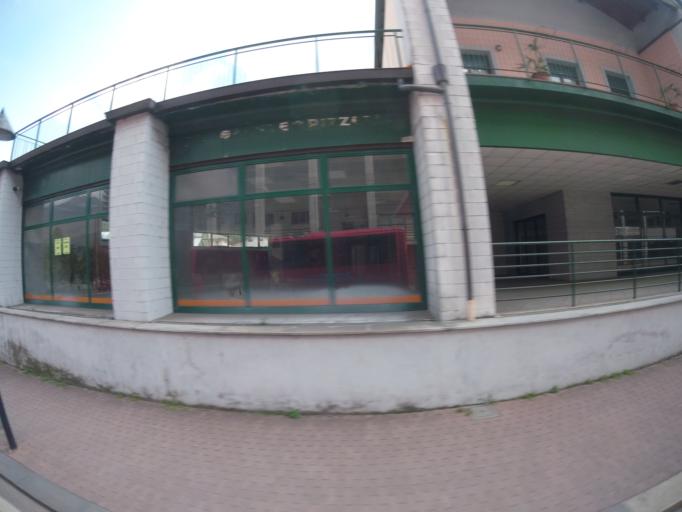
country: IT
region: Piedmont
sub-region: Provincia Verbano-Cusio-Ossola
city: Omegna
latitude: 45.8804
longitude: 8.4119
